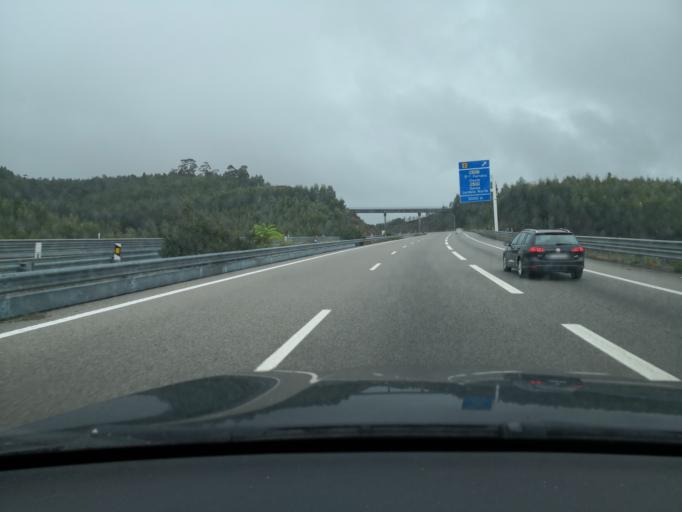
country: PT
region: Porto
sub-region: Valongo
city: Sobrado
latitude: 41.2352
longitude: -8.4471
